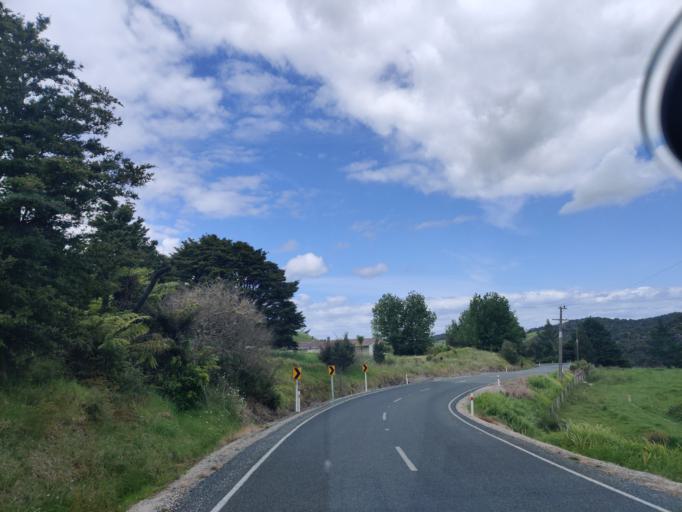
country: NZ
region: Northland
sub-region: Far North District
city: Kaitaia
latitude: -35.2862
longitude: 173.4861
